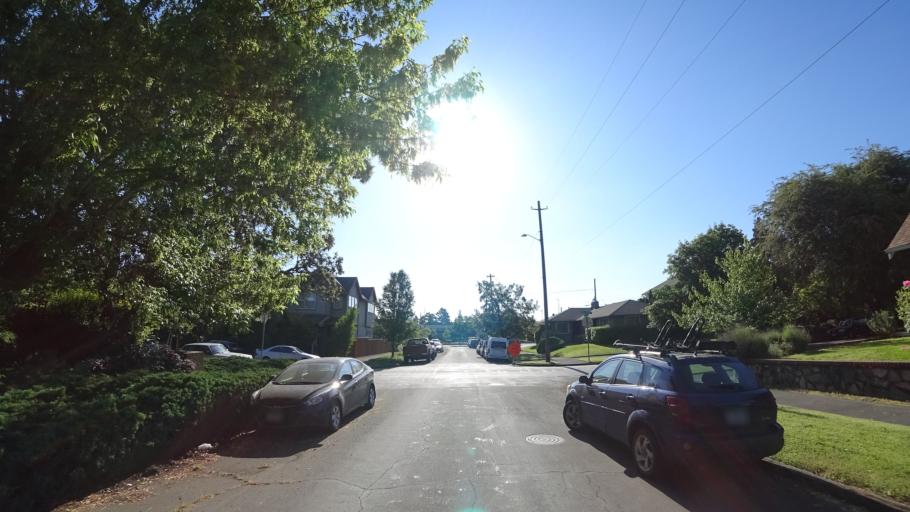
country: US
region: Oregon
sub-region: Multnomah County
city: Portland
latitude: 45.5690
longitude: -122.6630
